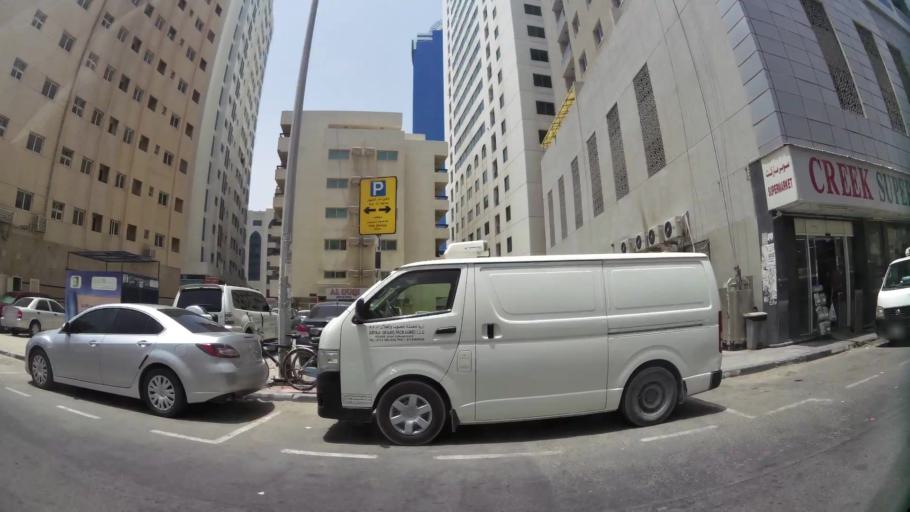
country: AE
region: Ash Shariqah
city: Sharjah
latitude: 25.3529
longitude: 55.3862
